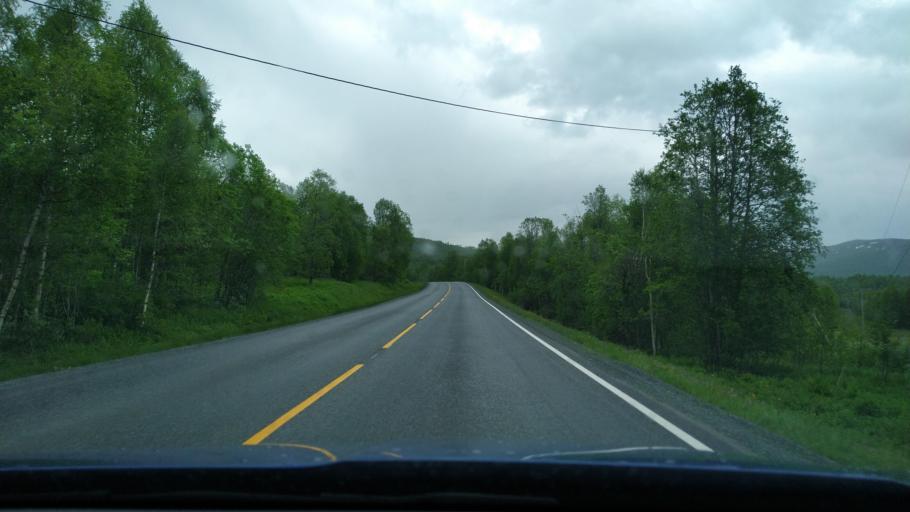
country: NO
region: Troms
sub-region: Malselv
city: Moen
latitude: 69.1094
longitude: 18.8567
